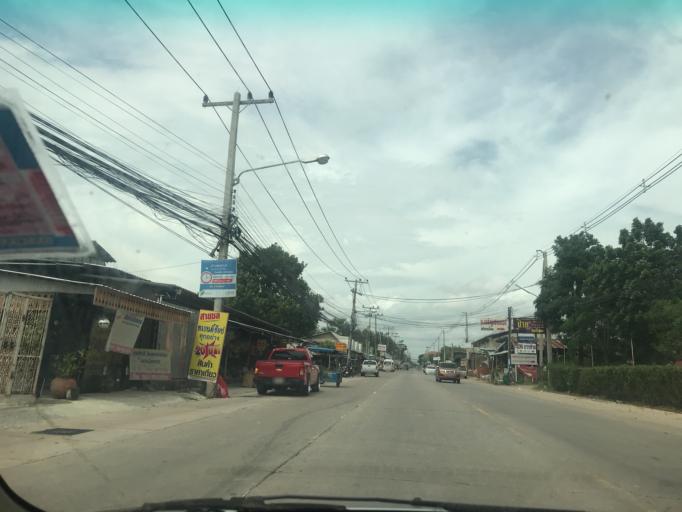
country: TH
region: Chon Buri
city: Phatthaya
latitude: 12.8828
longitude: 100.9078
